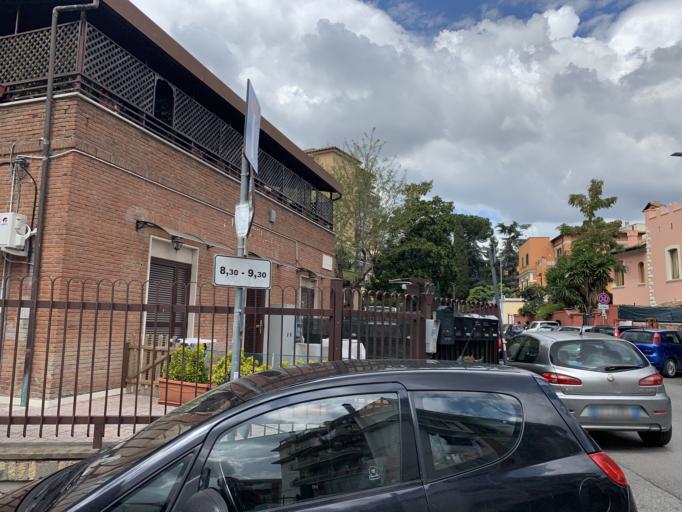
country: VA
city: Vatican City
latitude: 41.8811
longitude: 12.4242
